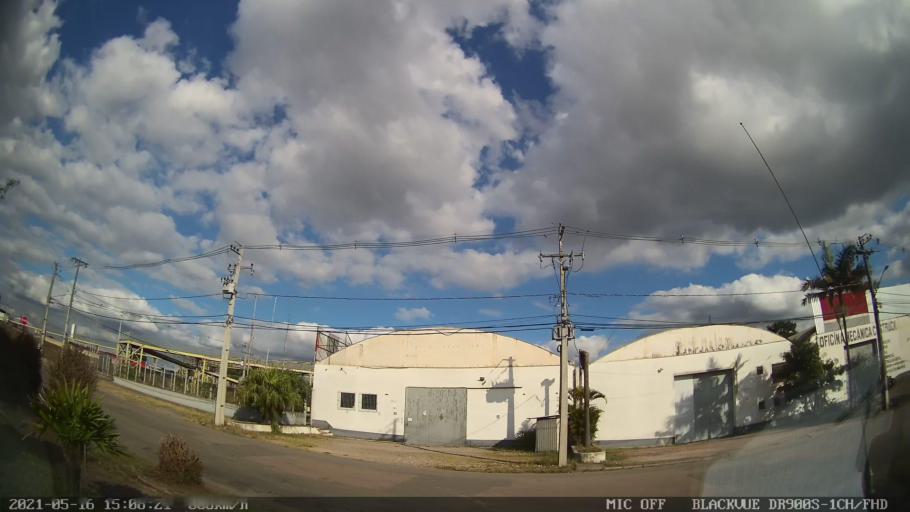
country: BR
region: Parana
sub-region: Sao Jose Dos Pinhais
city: Sao Jose dos Pinhais
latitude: -25.5567
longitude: -49.3050
